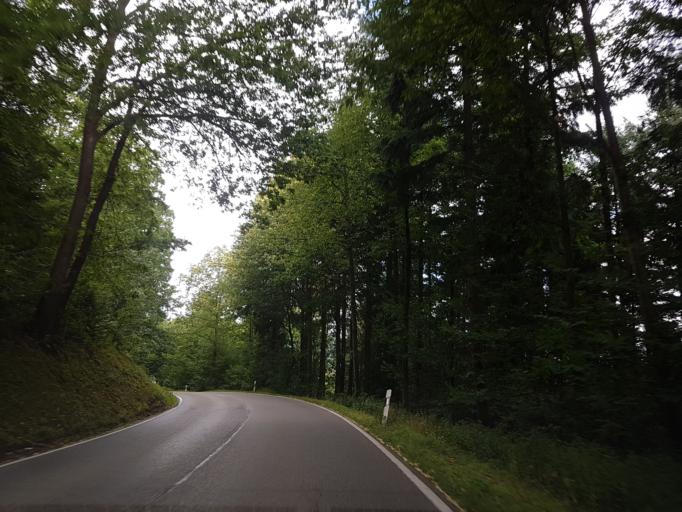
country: DE
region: Baden-Wuerttemberg
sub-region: Karlsruhe Region
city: Loffenau
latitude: 48.7675
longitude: 8.3660
